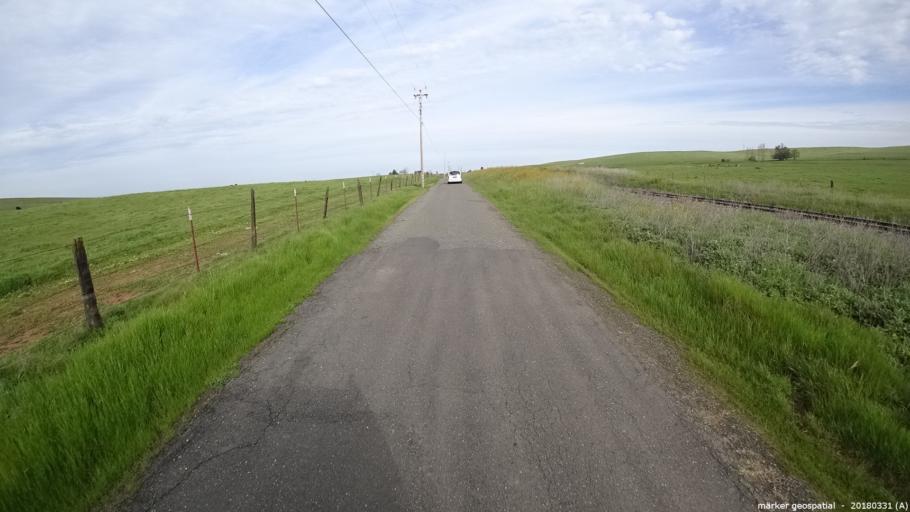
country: US
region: California
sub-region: El Dorado County
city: El Dorado Hills
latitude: 38.6240
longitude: -121.0873
